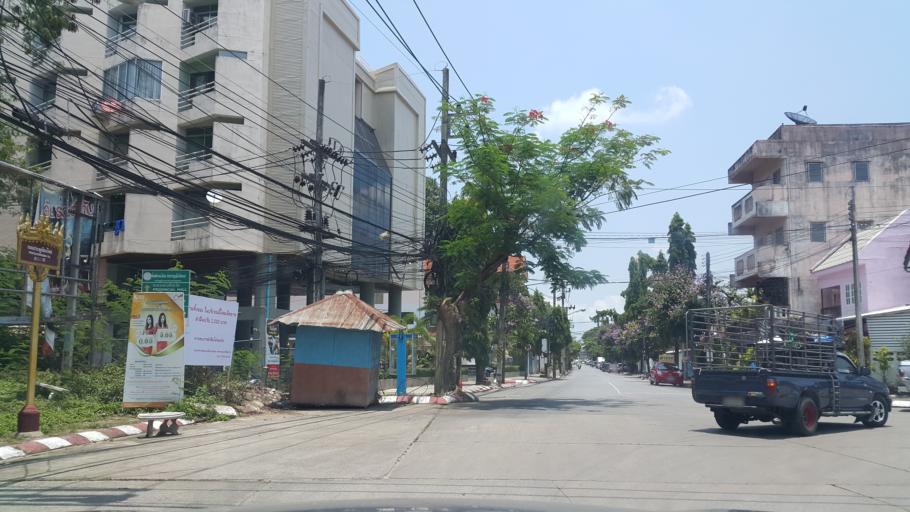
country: TH
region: Chiang Rai
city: Chiang Rai
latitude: 19.9090
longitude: 99.8237
